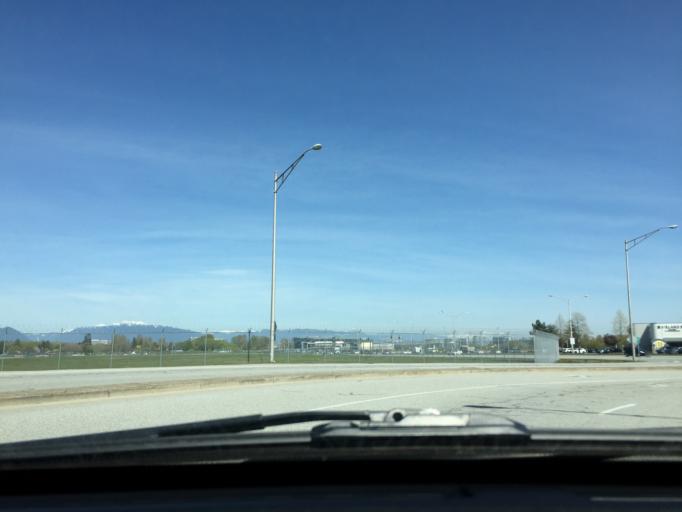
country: CA
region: British Columbia
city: Richmond
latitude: 49.1800
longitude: -123.1546
